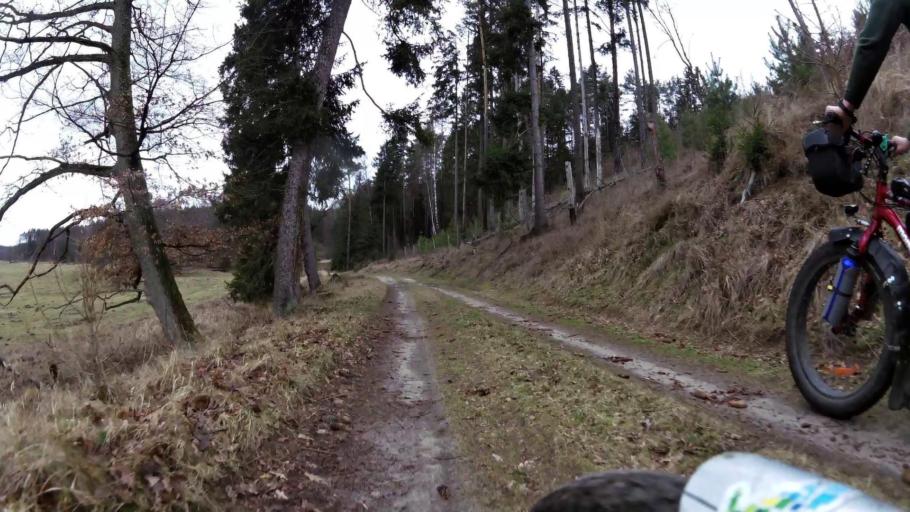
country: PL
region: Pomeranian Voivodeship
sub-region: Powiat bytowski
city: Kolczyglowy
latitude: 54.2508
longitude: 17.2963
